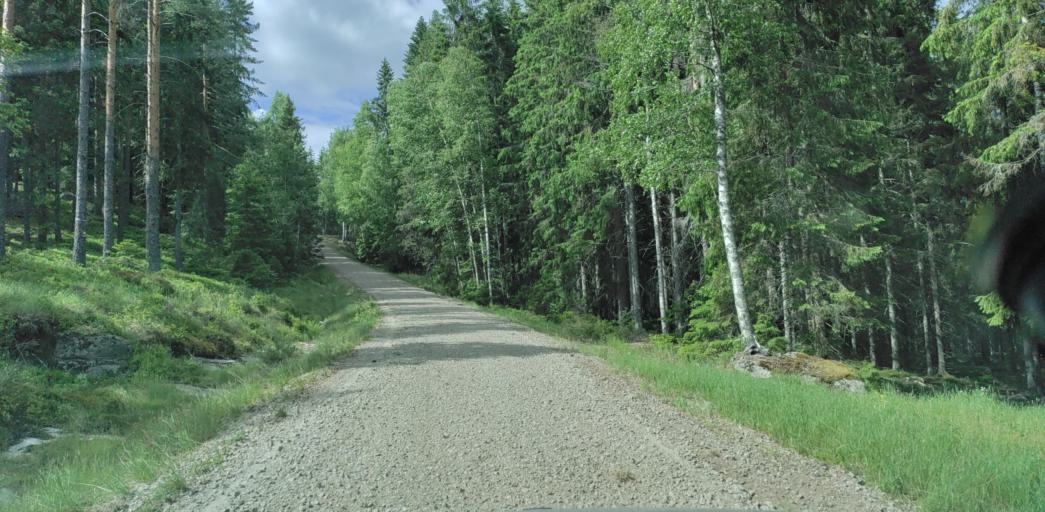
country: SE
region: Vaermland
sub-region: Munkfors Kommun
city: Munkfors
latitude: 59.9679
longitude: 13.4125
